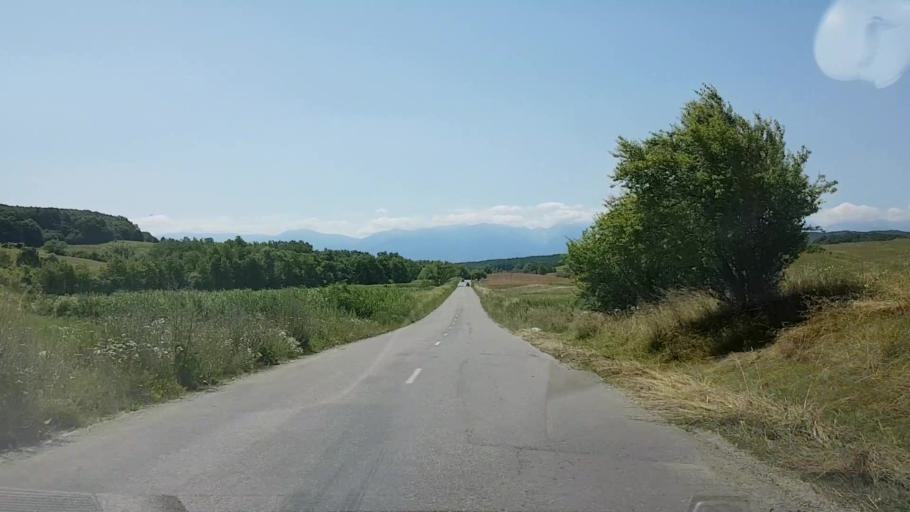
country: RO
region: Brasov
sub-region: Comuna Cincu
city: Cincu
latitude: 45.9027
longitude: 24.8118
